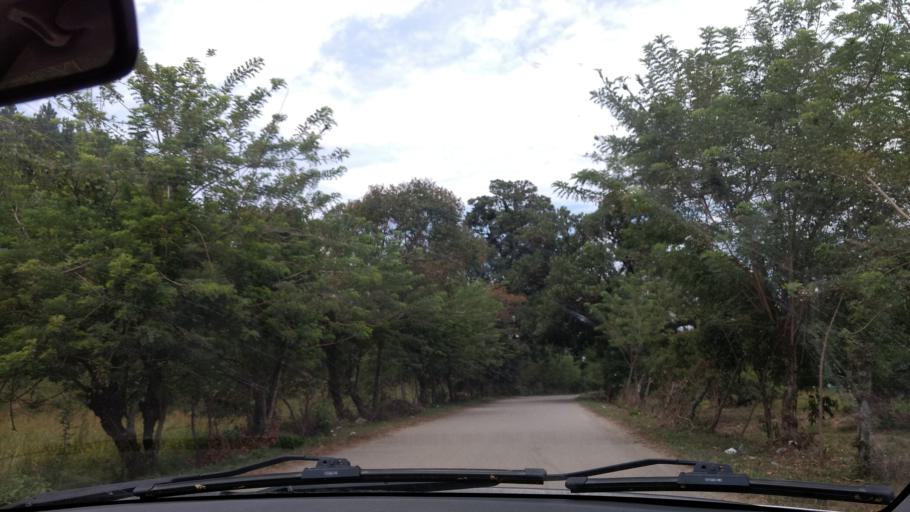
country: CO
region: Cauca
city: Buenos Aires
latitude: 3.0784
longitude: -76.6498
